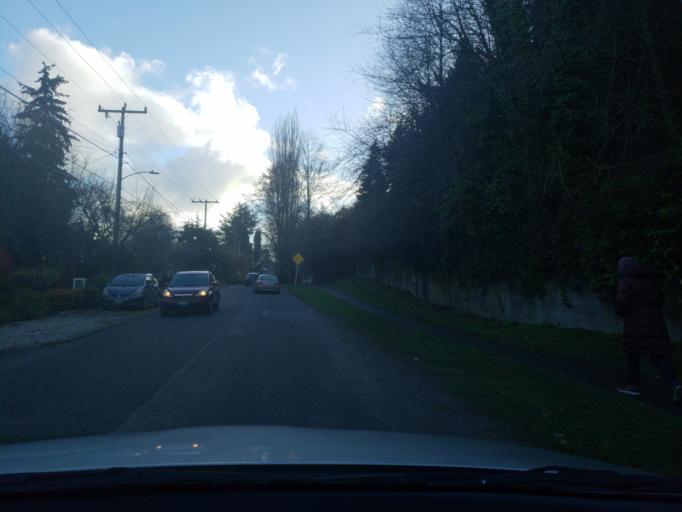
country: US
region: Washington
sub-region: King County
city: Seattle
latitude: 47.6571
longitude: -122.4036
